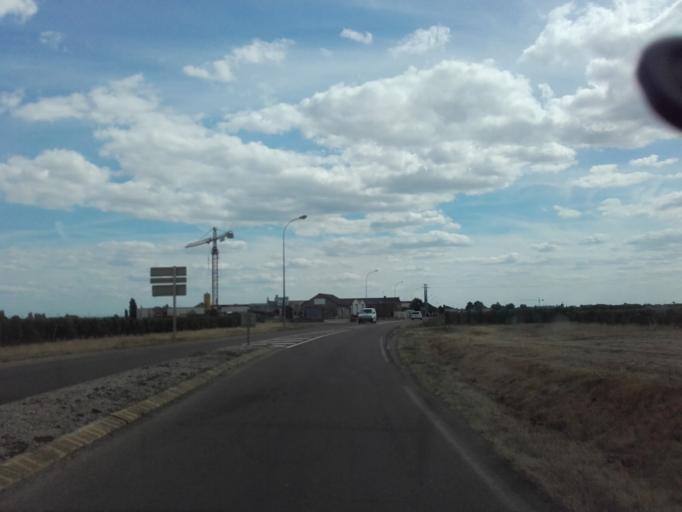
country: FR
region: Bourgogne
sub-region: Departement de la Cote-d'Or
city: Beaune
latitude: 47.0528
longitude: 4.8389
